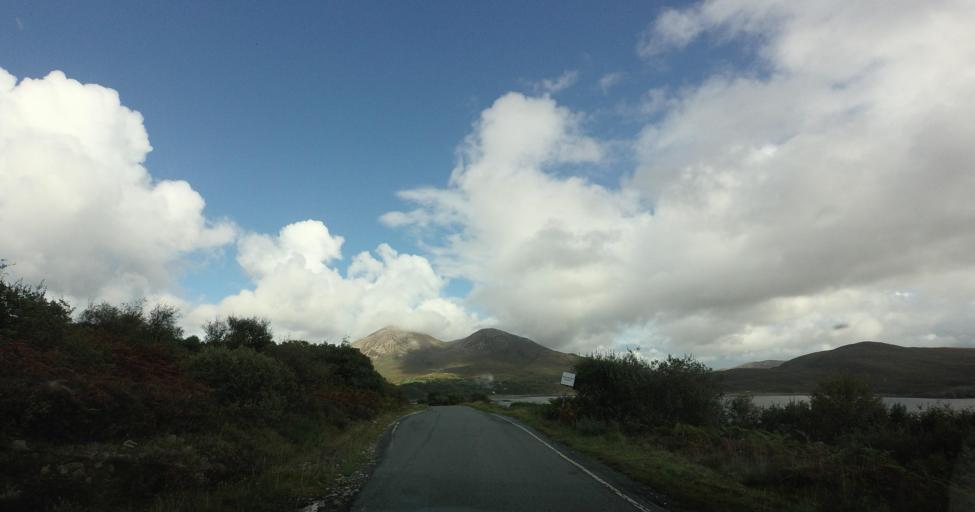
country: GB
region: Scotland
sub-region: Highland
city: Portree
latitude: 57.1950
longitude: -6.0294
